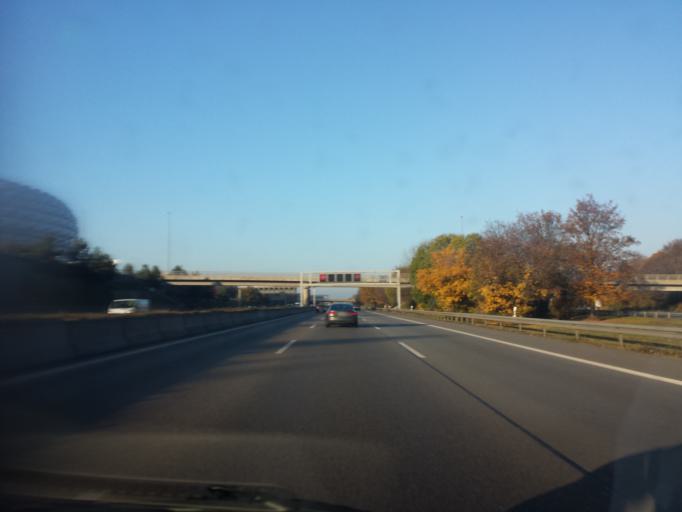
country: DE
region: Bavaria
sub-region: Upper Bavaria
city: Unterfoehring
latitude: 48.2157
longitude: 11.6266
